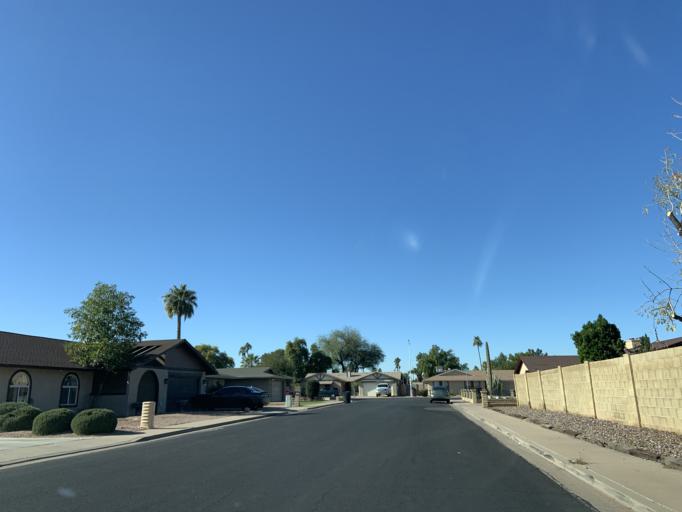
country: US
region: Arizona
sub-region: Maricopa County
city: San Carlos
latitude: 33.3655
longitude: -111.8634
